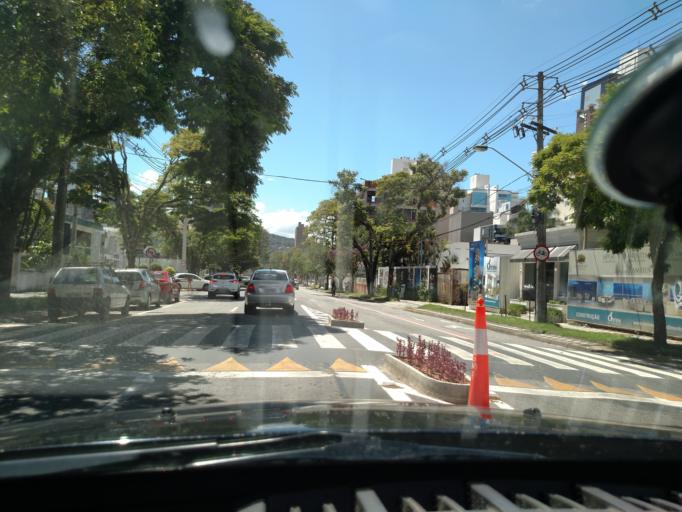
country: BR
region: Santa Catarina
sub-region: Blumenau
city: Blumenau
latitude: -26.9277
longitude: -49.0619
